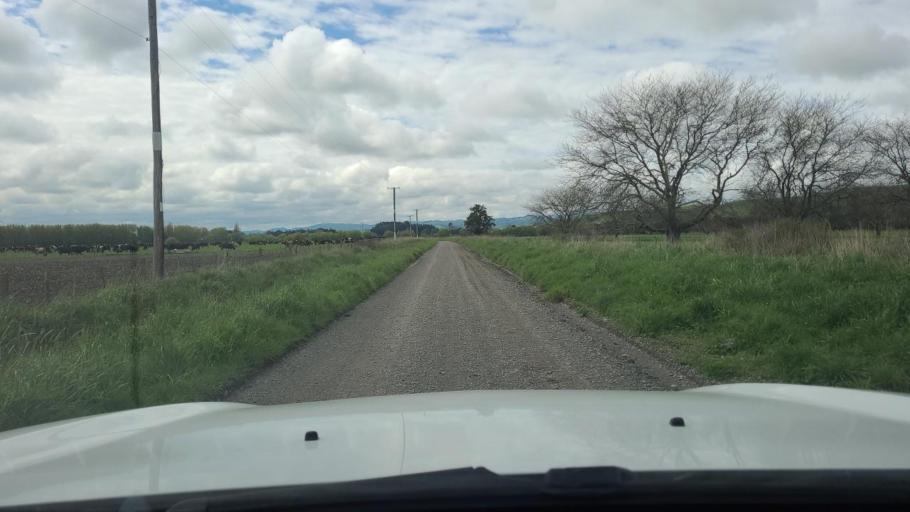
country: NZ
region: Wellington
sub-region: Masterton District
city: Masterton
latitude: -41.0959
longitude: 175.4975
